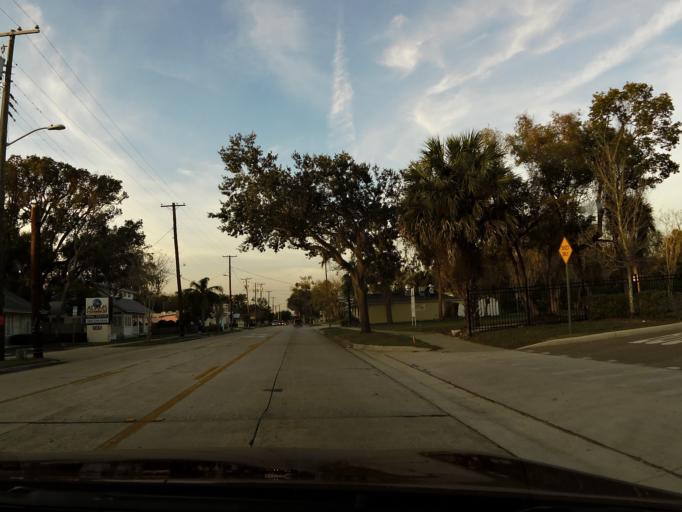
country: US
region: Florida
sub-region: Volusia County
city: DeLand
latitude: 29.0216
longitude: -81.3032
